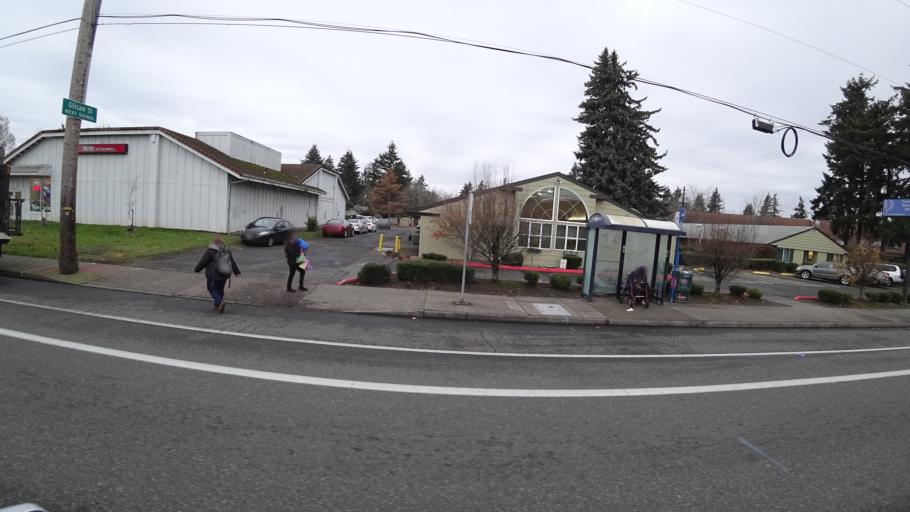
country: US
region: Oregon
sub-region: Multnomah County
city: Lents
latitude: 45.5277
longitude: -122.5378
